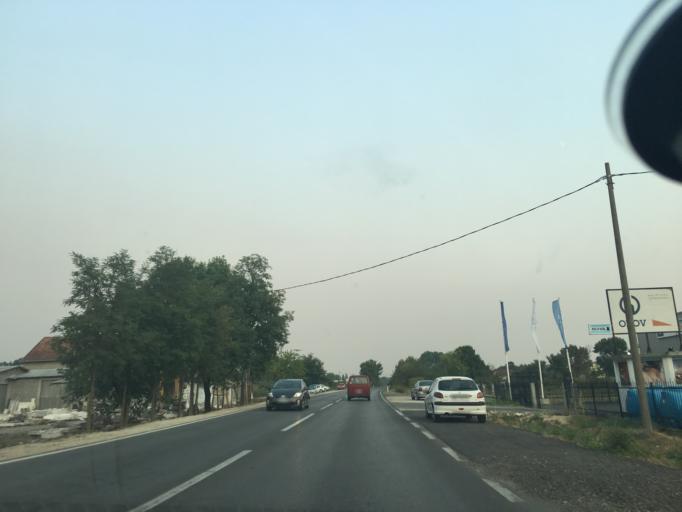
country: ME
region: Danilovgrad
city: Danilovgrad
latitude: 42.5443
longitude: 19.1050
